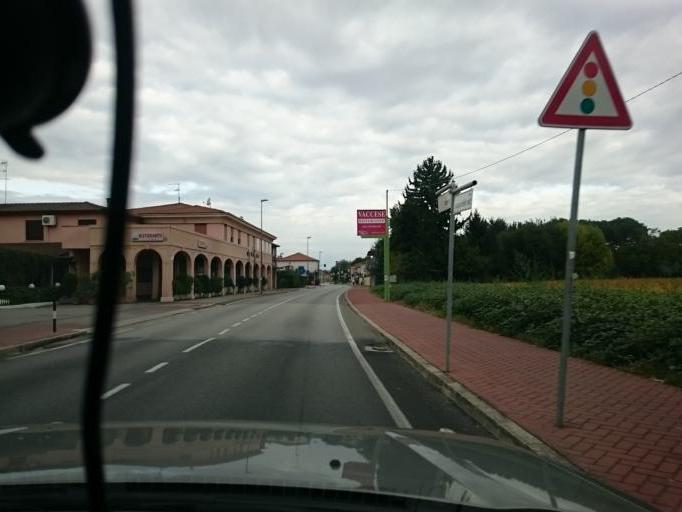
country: IT
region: Veneto
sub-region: Provincia di Padova
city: Saccolongo
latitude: 45.4022
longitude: 11.7498
